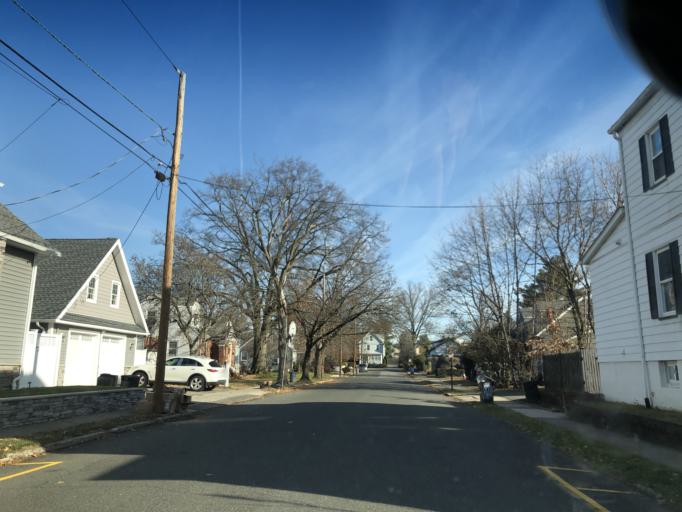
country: US
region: New Jersey
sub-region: Bergen County
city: Elmwood Park
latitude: 40.9210
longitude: -74.1255
